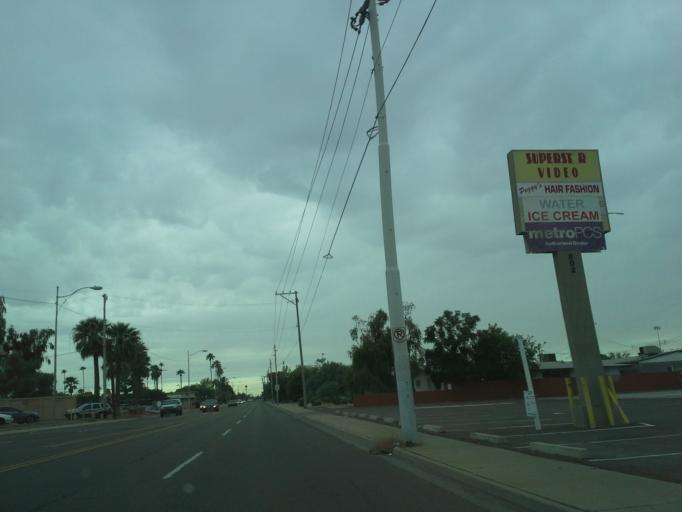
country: US
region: Arizona
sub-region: Maricopa County
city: Phoenix
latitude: 33.4877
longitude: -112.0838
